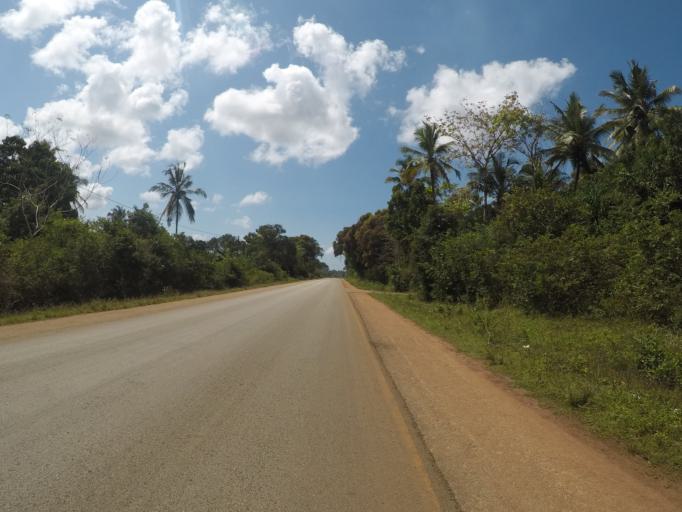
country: TZ
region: Zanzibar Central/South
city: Koani
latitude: -6.1670
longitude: 39.3303
